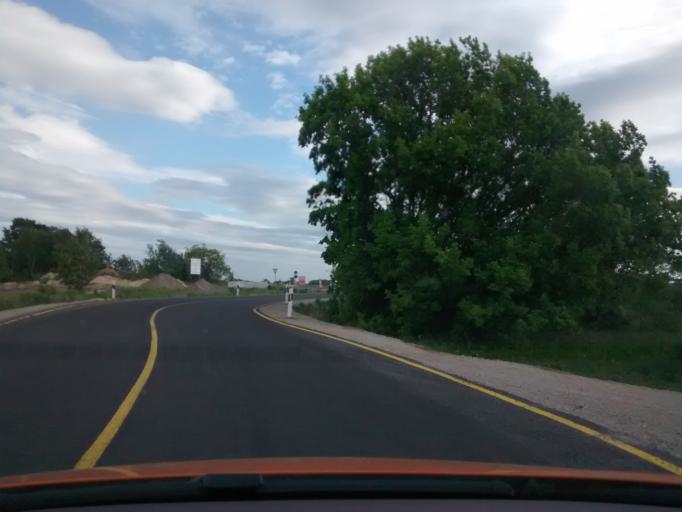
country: DE
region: Brandenburg
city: Schulzendorf
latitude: 52.3701
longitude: 13.5498
